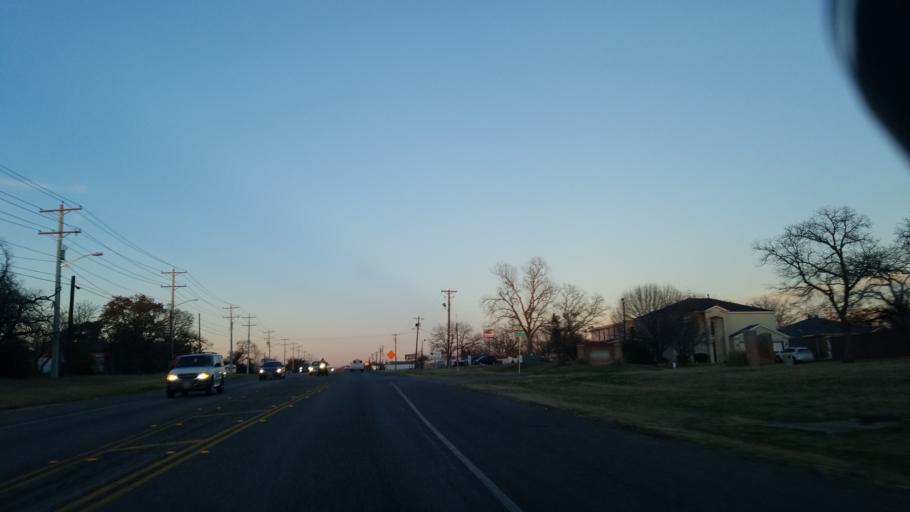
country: US
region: Texas
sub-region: Denton County
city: Denton
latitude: 33.1708
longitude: -97.1494
